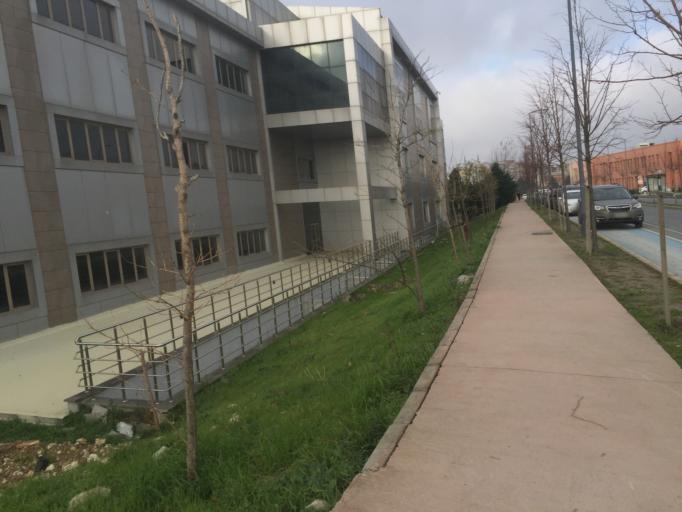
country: TR
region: Istanbul
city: merter keresteciler
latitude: 41.0281
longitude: 28.8934
